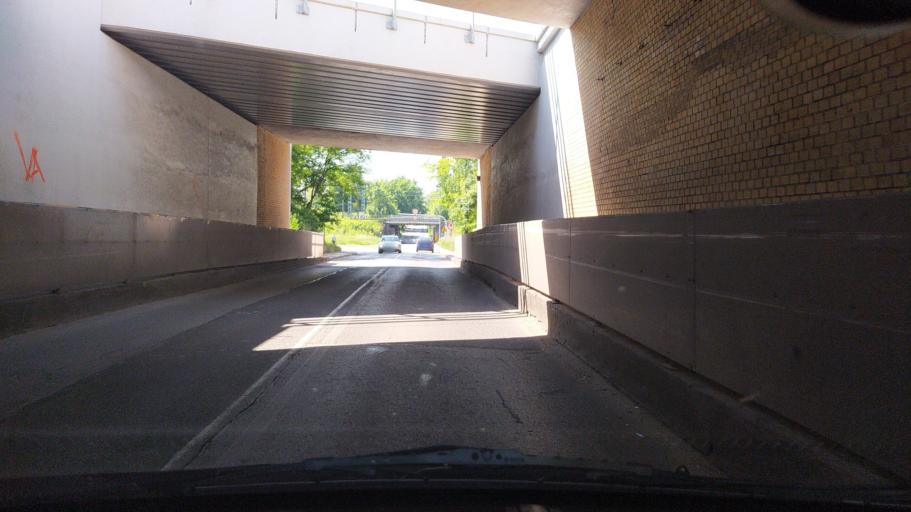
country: PL
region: Silesian Voivodeship
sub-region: Powiat gliwicki
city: Przyszowice
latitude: 50.2973
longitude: 18.7323
